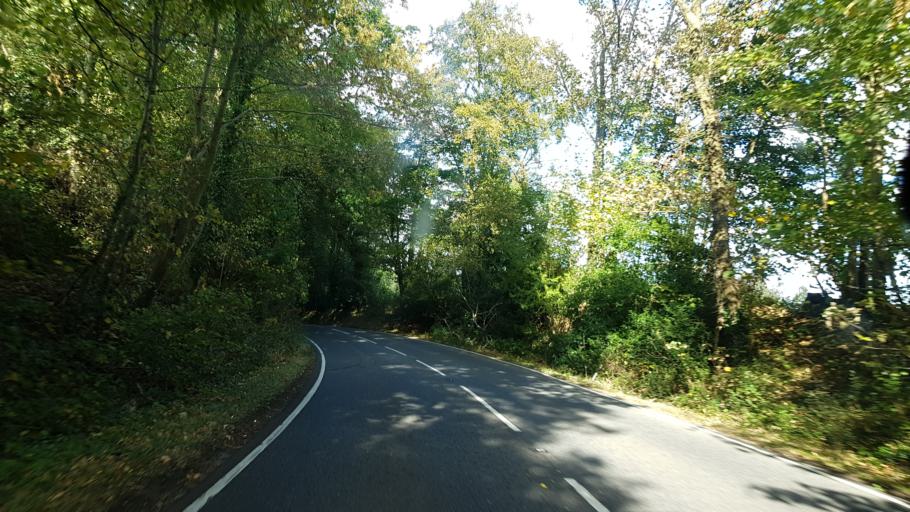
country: GB
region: England
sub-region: Surrey
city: Chiddingfold
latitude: 51.1009
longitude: -0.6338
